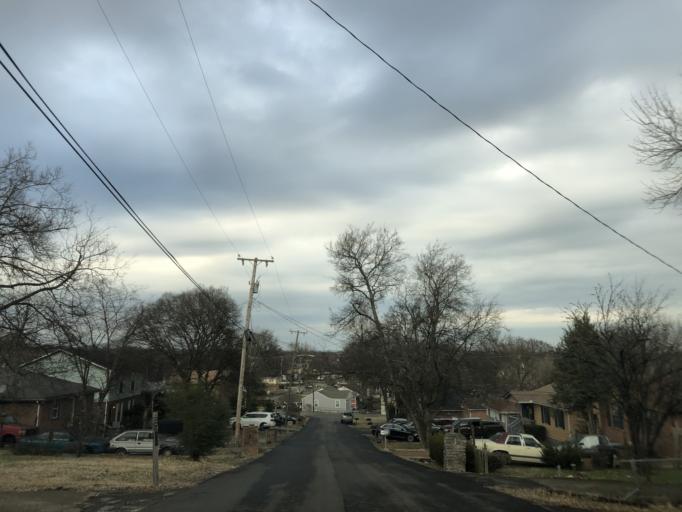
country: US
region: Tennessee
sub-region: Davidson County
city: Nashville
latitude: 36.2000
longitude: -86.7290
